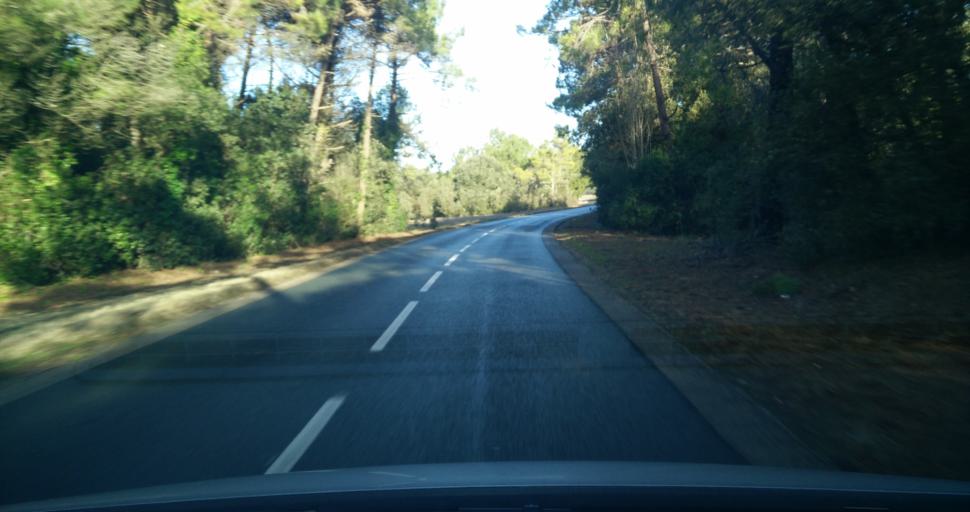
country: FR
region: Poitou-Charentes
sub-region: Departement de la Charente-Maritime
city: La Flotte
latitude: 46.1730
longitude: -1.3292
